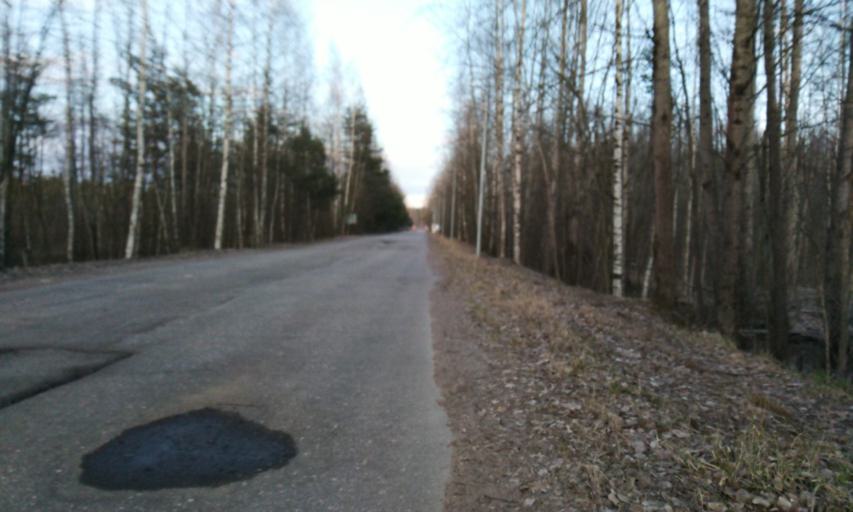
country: RU
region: Leningrad
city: Novoye Devyatkino
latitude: 60.0783
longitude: 30.4870
